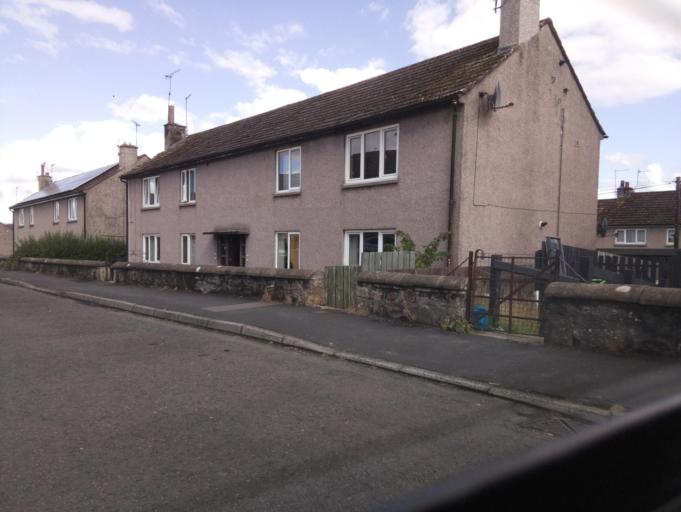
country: GB
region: Scotland
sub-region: Stirling
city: Dunblane
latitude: 56.1849
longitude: -3.9717
